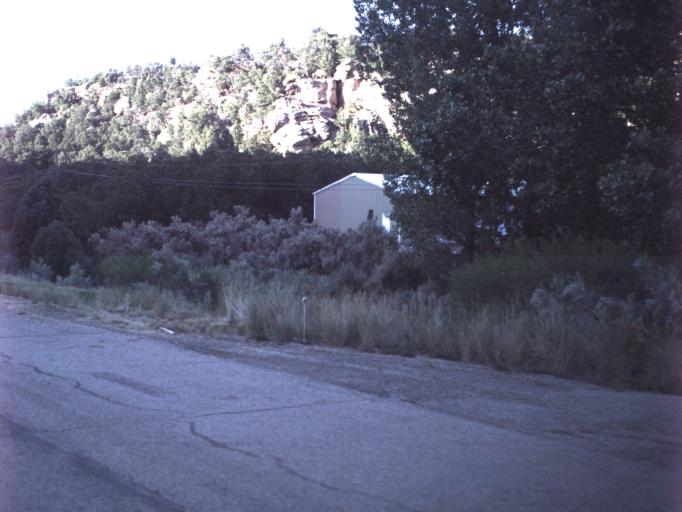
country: US
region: Utah
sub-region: San Juan County
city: Monticello
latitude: 37.9780
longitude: -109.3553
